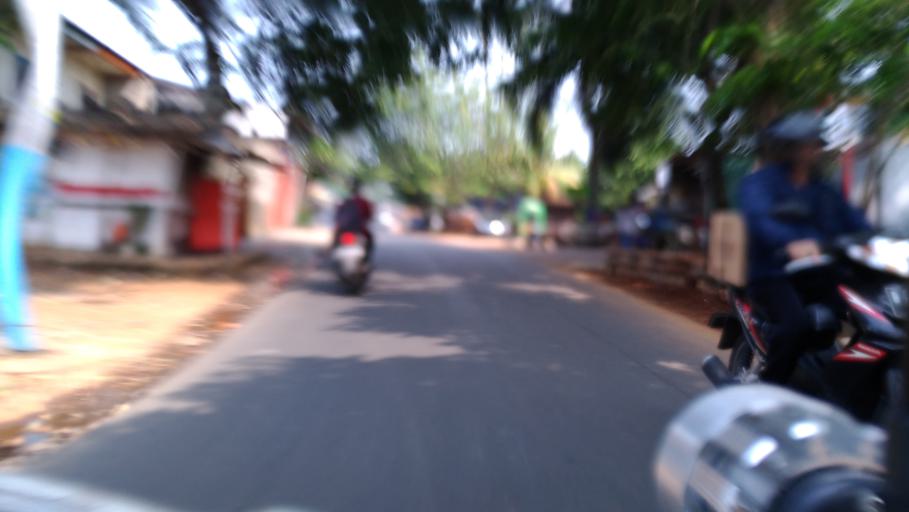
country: ID
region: West Java
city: Depok
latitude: -6.3521
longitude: 106.8783
